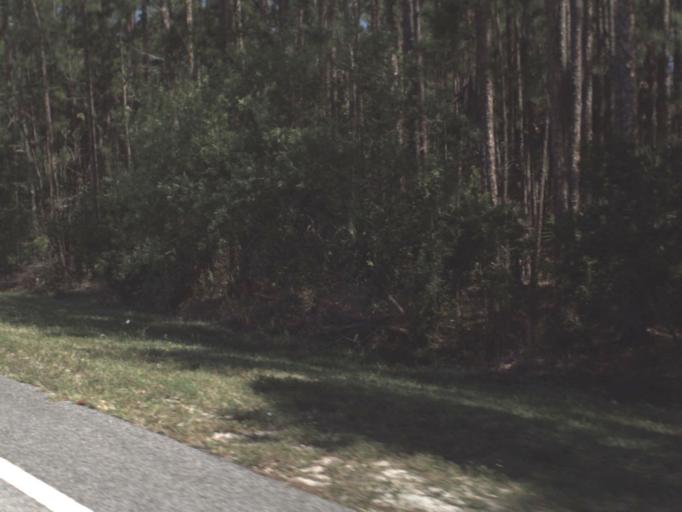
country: US
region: Florida
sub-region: Volusia County
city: Ormond-by-the-Sea
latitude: 29.3707
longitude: -81.1753
